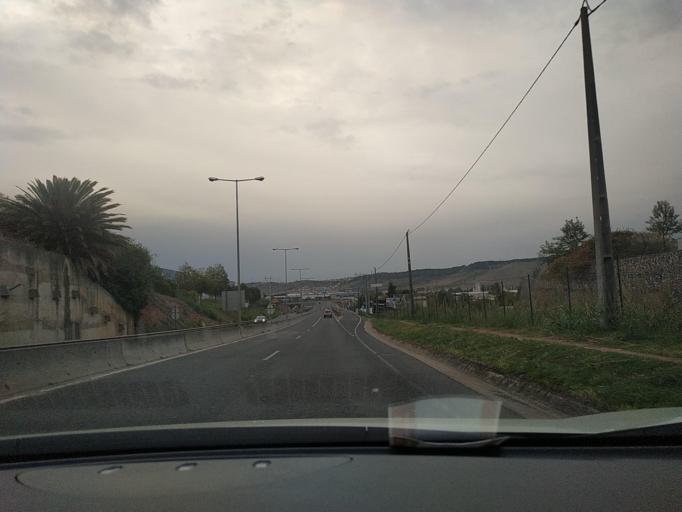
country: PT
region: Lisbon
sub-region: Loures
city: Santo Antao do Tojal
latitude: 38.8611
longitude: -9.1222
